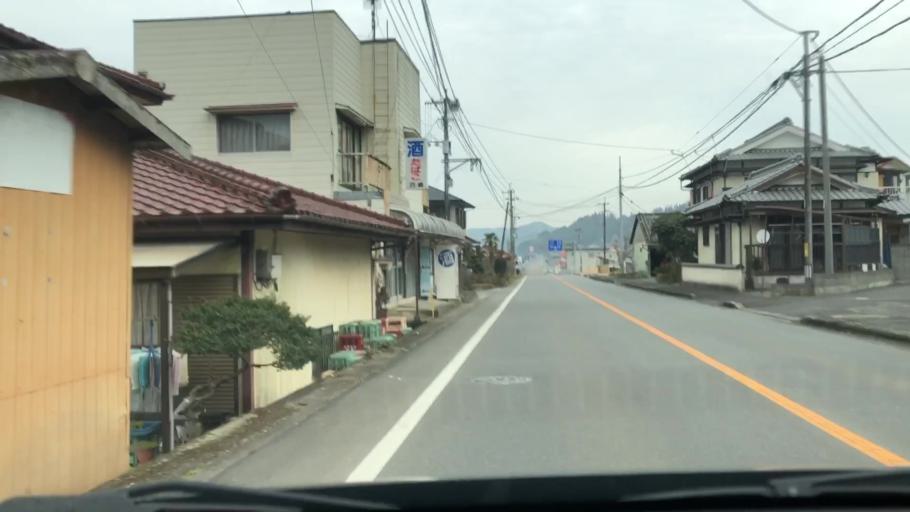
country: JP
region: Oita
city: Usuki
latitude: 33.0299
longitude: 131.6880
